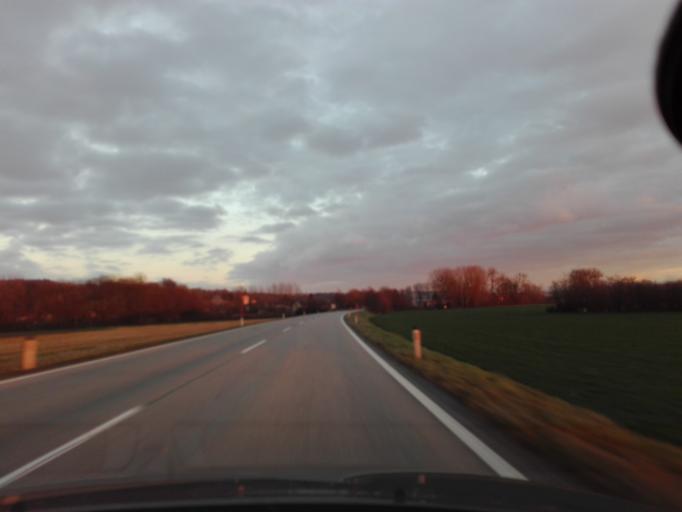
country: AT
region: Upper Austria
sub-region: Politischer Bezirk Perg
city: Bad Kreuzen
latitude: 48.2100
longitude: 14.7789
